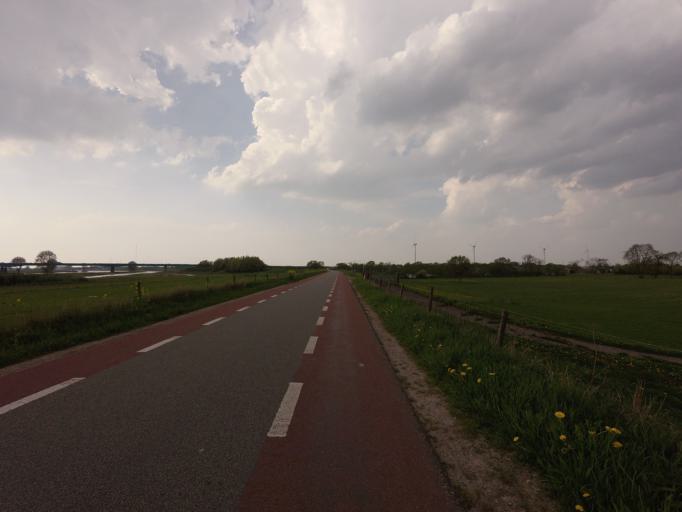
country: NL
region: Utrecht
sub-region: Gemeente Vianen
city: Vianen
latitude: 52.0012
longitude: 5.1253
